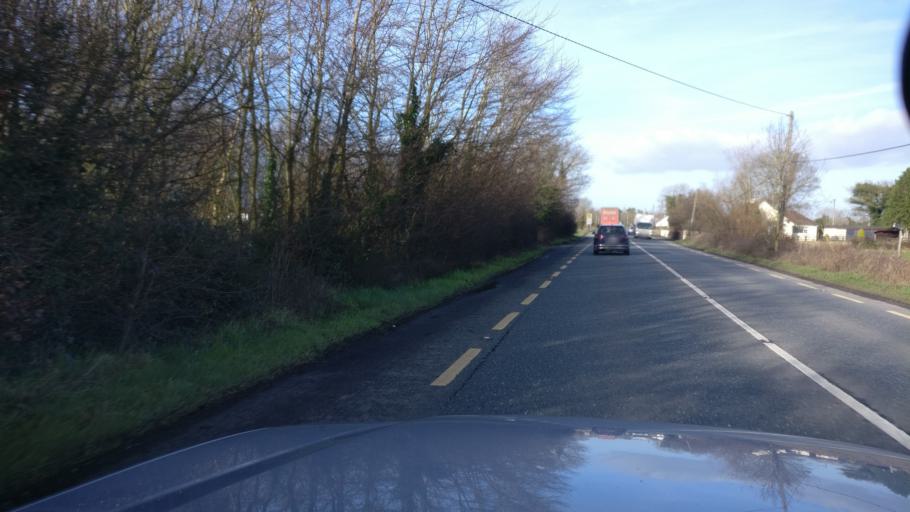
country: IE
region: Leinster
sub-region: Uibh Fhaili
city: Tullamore
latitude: 53.2380
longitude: -7.4786
